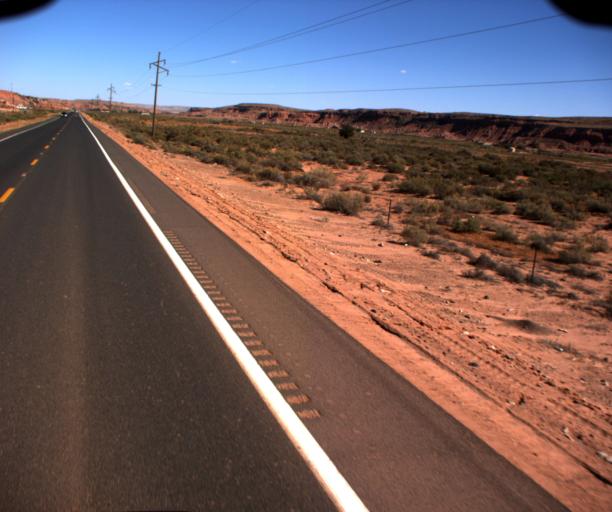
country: US
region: Arizona
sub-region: Coconino County
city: Tuba City
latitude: 36.1044
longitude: -111.2748
